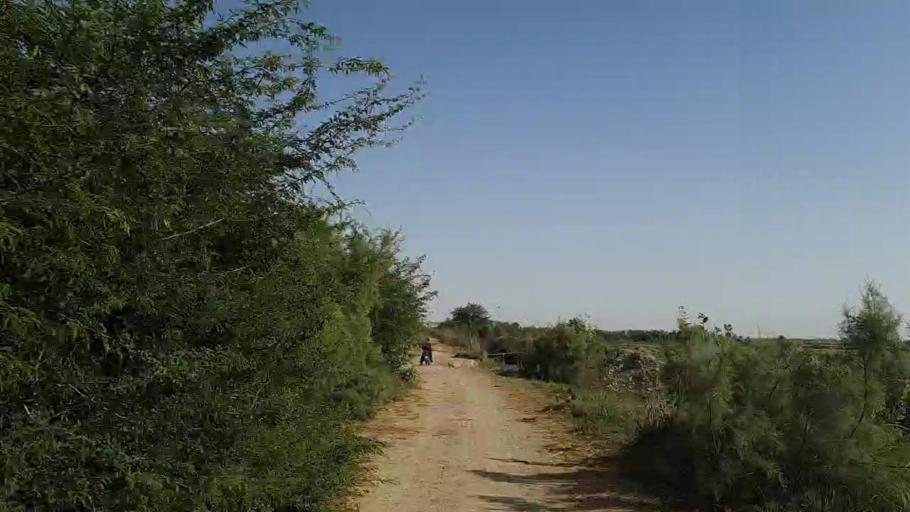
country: PK
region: Sindh
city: Chuhar Jamali
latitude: 24.4810
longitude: 68.1124
